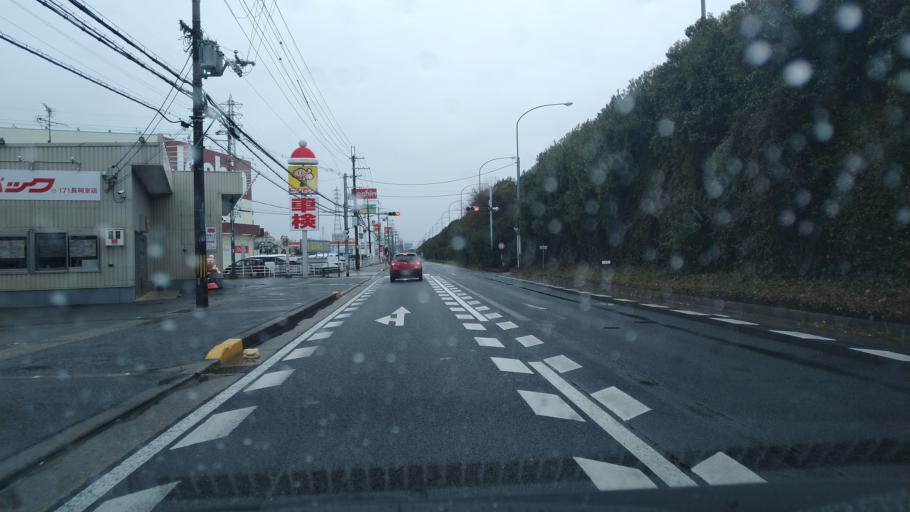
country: JP
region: Kyoto
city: Muko
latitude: 34.9236
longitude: 135.7104
